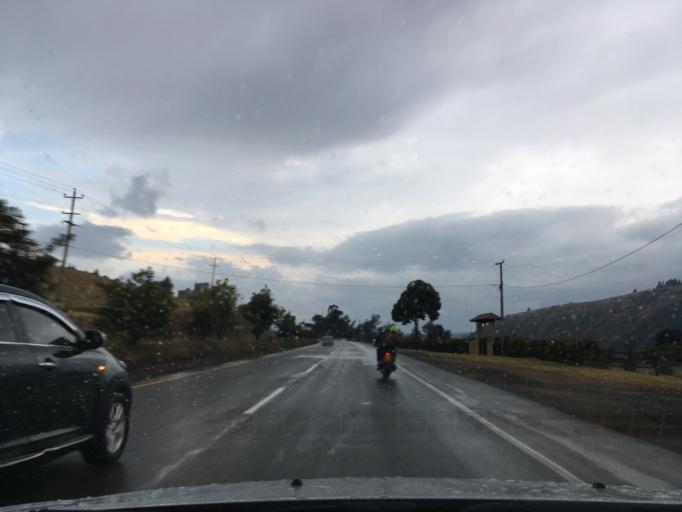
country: CO
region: Cundinamarca
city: Choconta
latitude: 5.1292
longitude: -73.6948
